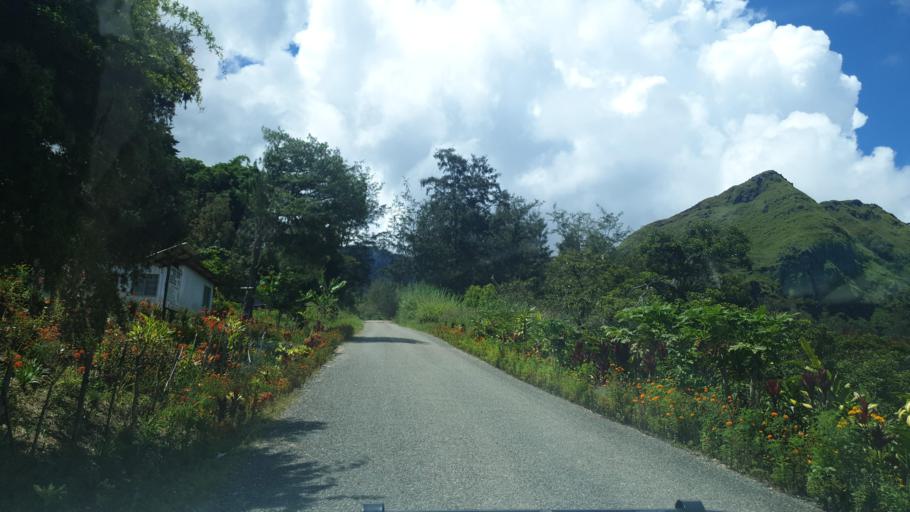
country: PG
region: Chimbu
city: Kundiawa
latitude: -6.1444
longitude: 145.1315
